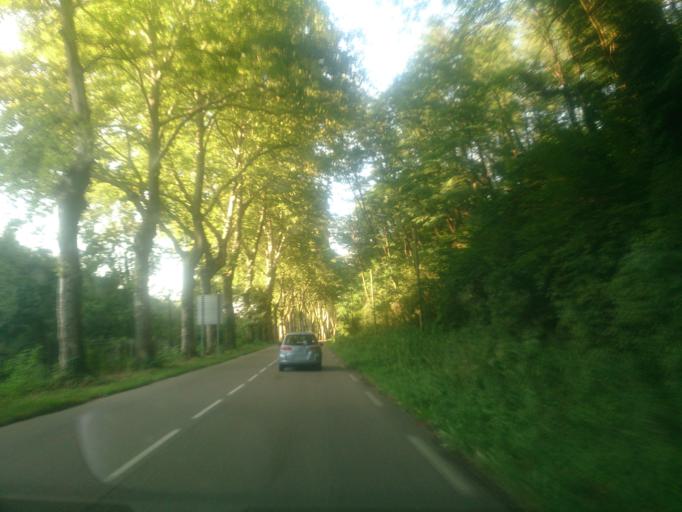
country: FR
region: Limousin
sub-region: Departement de la Correze
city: Brive-la-Gaillarde
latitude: 45.1271
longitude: 1.5173
